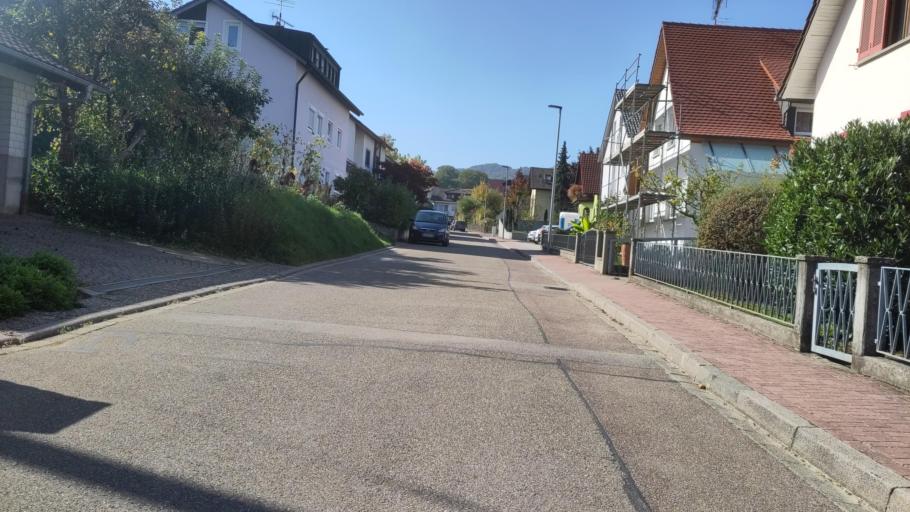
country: DE
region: Baden-Wuerttemberg
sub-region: Freiburg Region
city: Bahlingen
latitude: 48.1184
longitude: 7.7295
